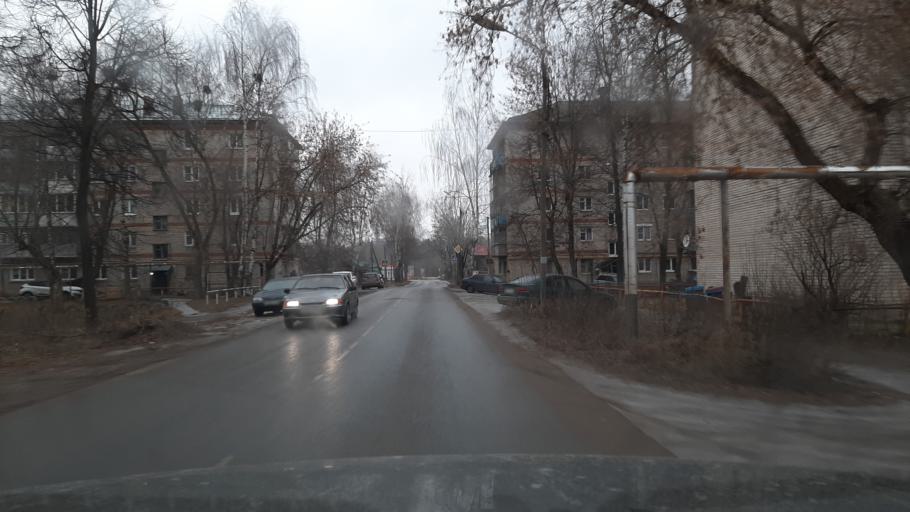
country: RU
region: Ivanovo
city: Shuya
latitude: 56.8542
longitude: 41.3571
